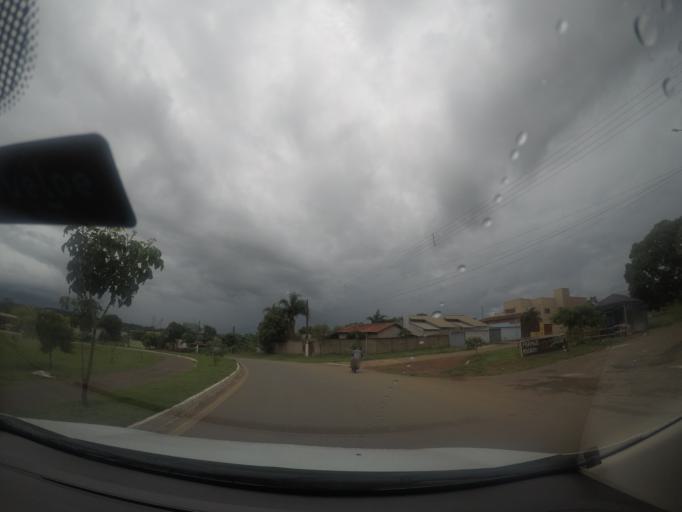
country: BR
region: Goias
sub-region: Trindade
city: Trindade
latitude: -16.6330
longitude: -49.3884
